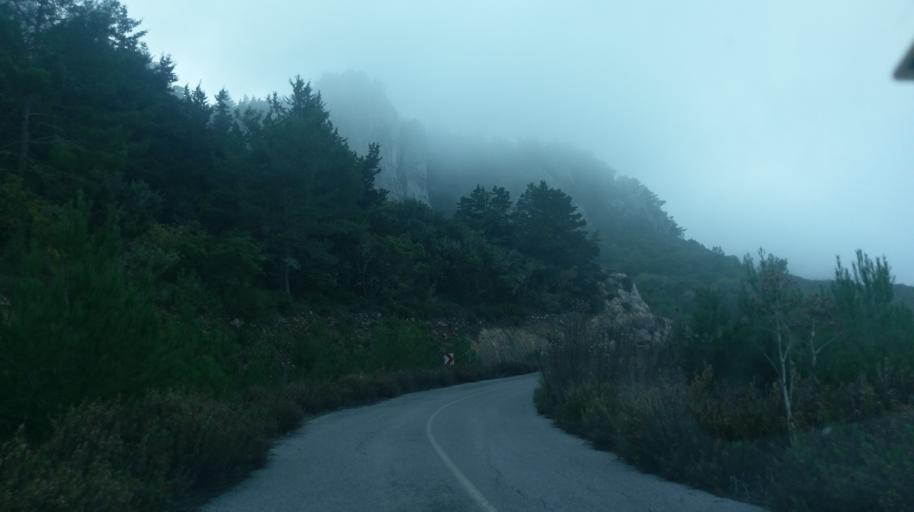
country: CY
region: Ammochostos
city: Trikomo
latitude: 35.3869
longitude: 33.8885
